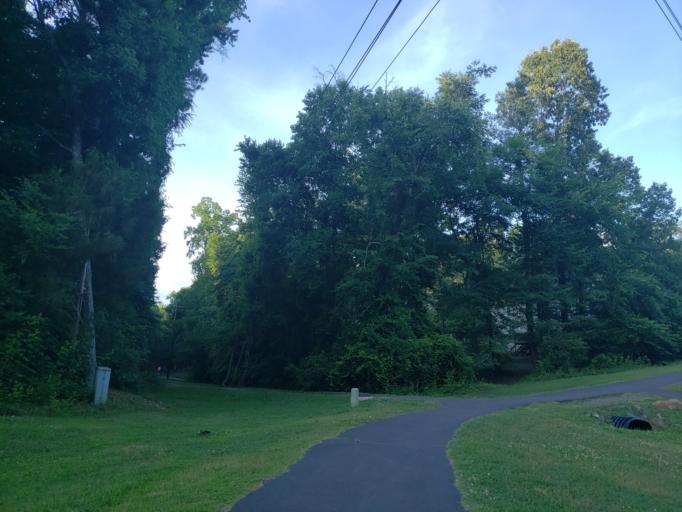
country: US
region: North Carolina
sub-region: Durham County
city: Durham
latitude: 35.9191
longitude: -78.9446
